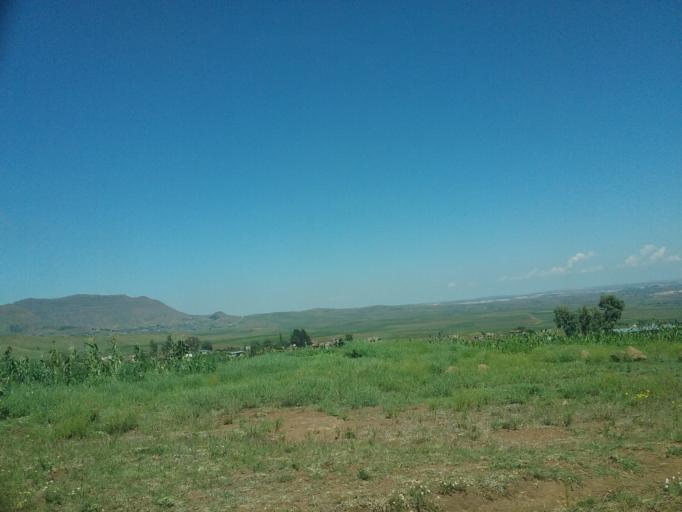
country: LS
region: Berea
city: Teyateyaneng
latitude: -29.2250
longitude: 27.8697
